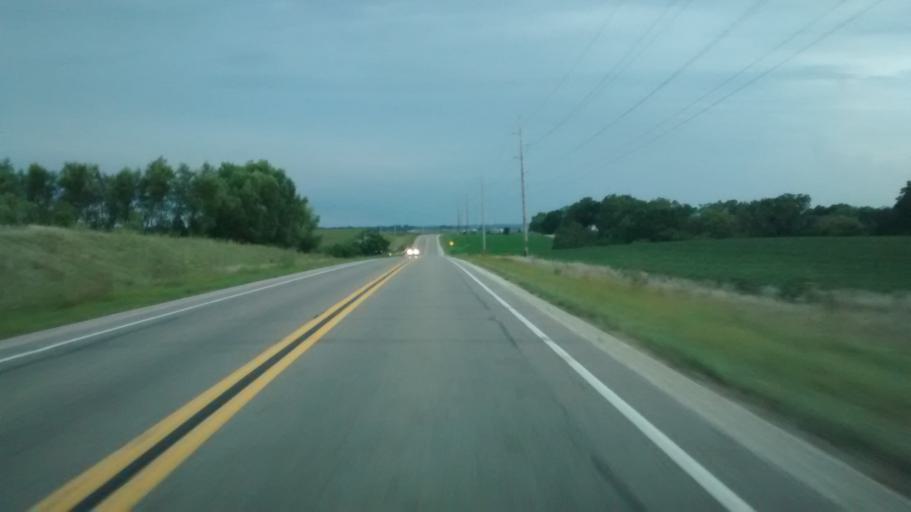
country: US
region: Iowa
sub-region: Woodbury County
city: Moville
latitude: 42.5145
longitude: -96.0515
